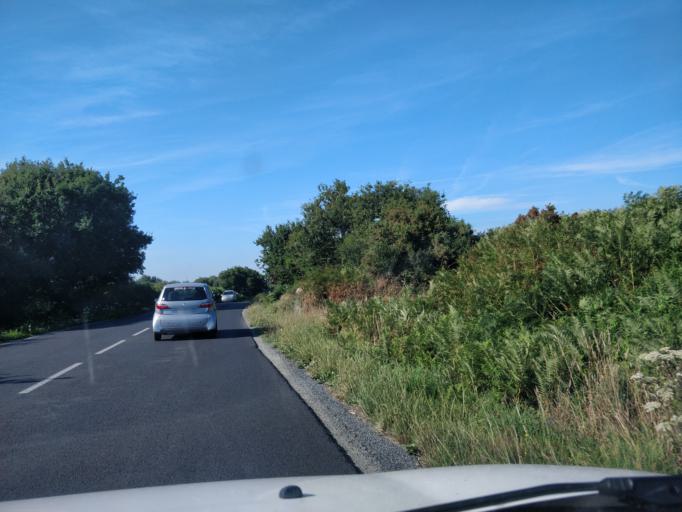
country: FR
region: Brittany
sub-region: Departement des Cotes-d'Armor
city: Tregastel
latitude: 48.7933
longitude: -3.4962
